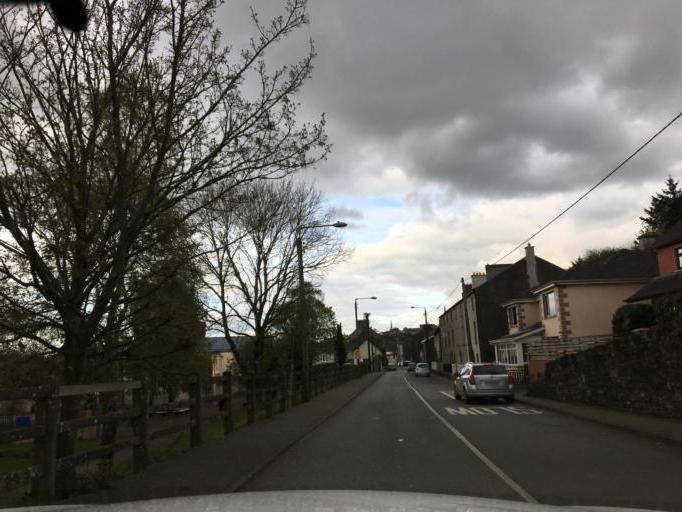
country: IE
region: Leinster
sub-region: Loch Garman
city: New Ross
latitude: 52.3901
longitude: -6.9484
